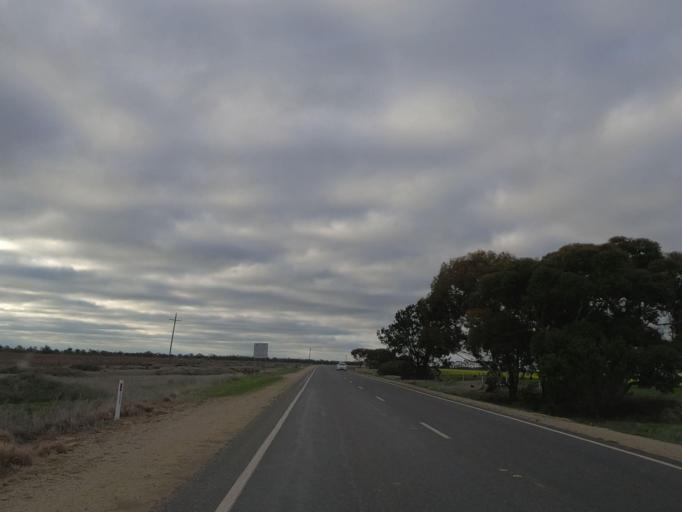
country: AU
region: Victoria
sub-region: Swan Hill
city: Swan Hill
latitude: -35.8305
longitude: 143.9444
